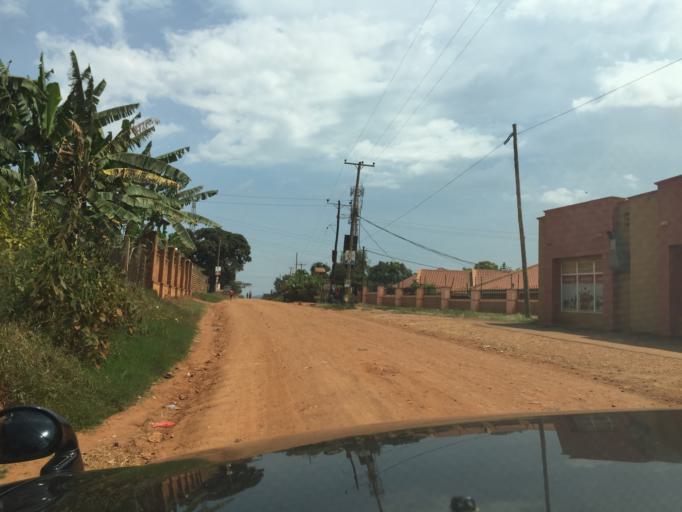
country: UG
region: Central Region
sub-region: Wakiso District
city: Kireka
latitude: 0.4063
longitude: 32.6199
